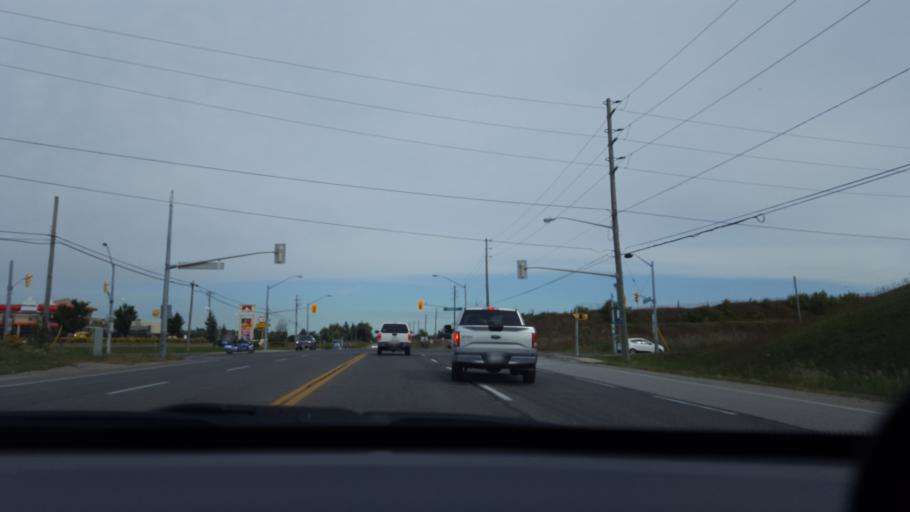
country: CA
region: Ontario
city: Vaughan
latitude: 43.8912
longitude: -79.5208
